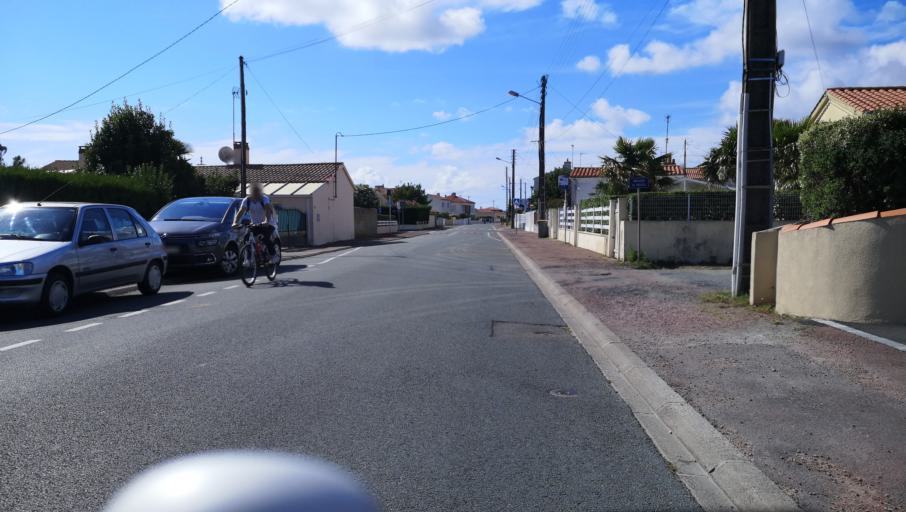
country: FR
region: Pays de la Loire
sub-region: Departement de la Vendee
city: Les Sables-d'Olonne
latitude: 46.5104
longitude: -1.7863
